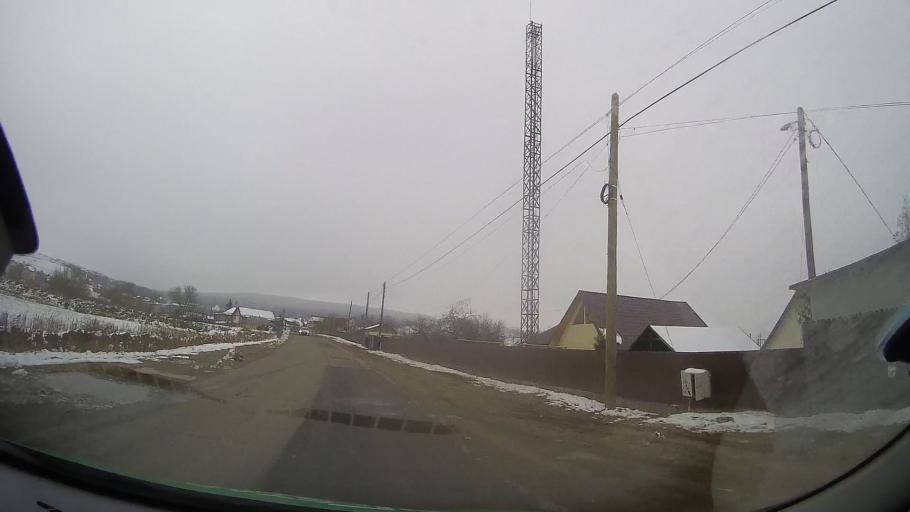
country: RO
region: Bacau
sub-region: Comuna Podu Turcului
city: Podu Turcului
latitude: 46.2062
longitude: 27.3808
